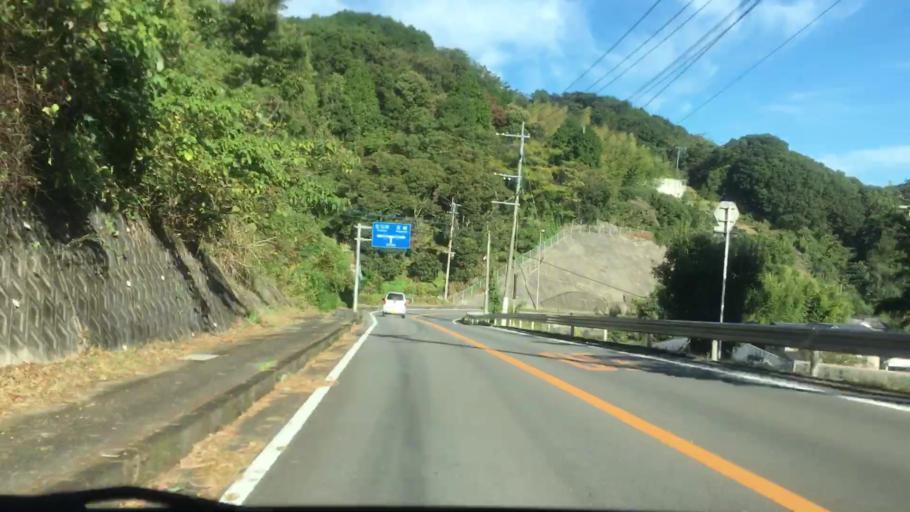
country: JP
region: Nagasaki
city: Sasebo
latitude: 33.0006
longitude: 129.7282
